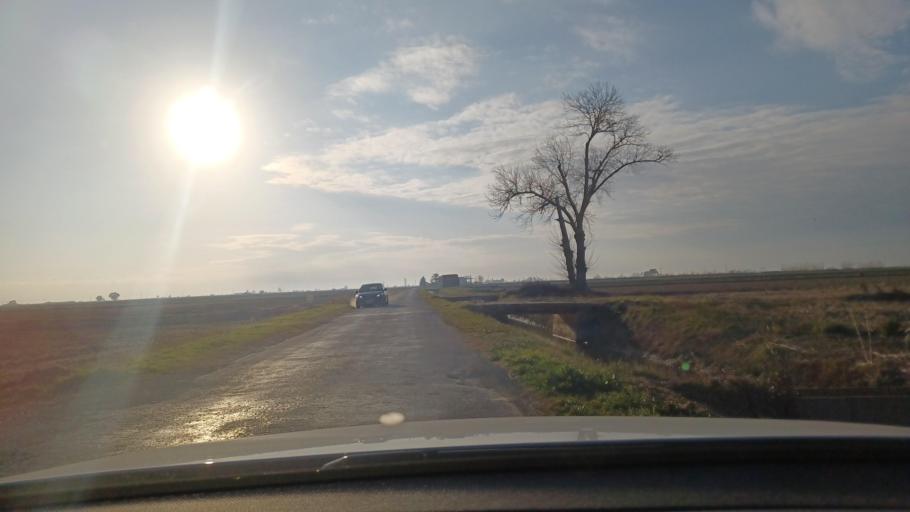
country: ES
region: Catalonia
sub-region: Provincia de Tarragona
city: Deltebre
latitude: 40.6876
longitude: 0.6528
